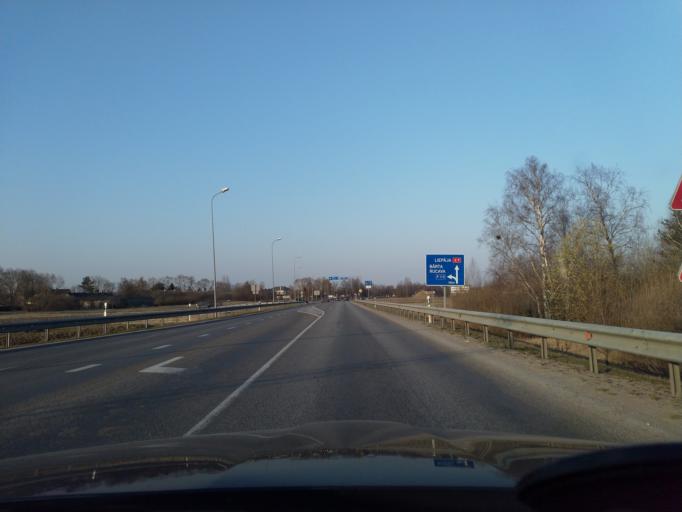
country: LV
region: Grobina
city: Grobina
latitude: 56.5397
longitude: 21.1554
